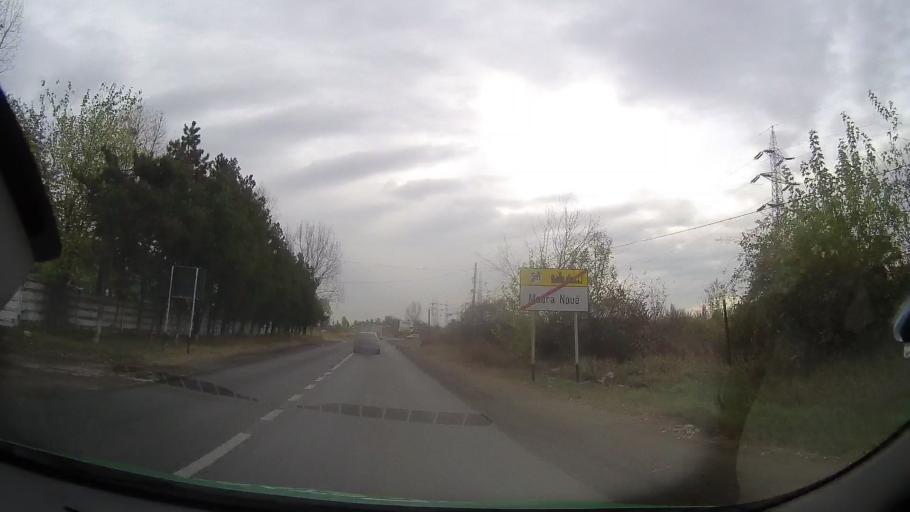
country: RO
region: Prahova
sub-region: Comuna Berceni
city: Berceni
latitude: 44.9437
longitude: 26.1008
